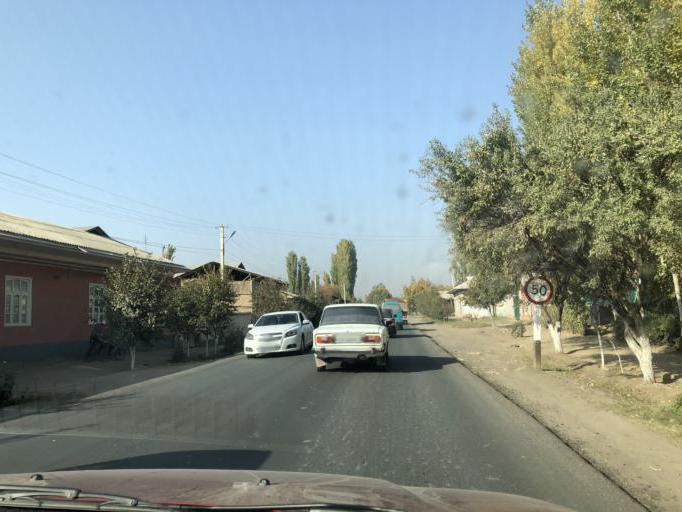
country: UZ
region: Namangan
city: Chust Shahri
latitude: 41.0694
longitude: 71.2046
